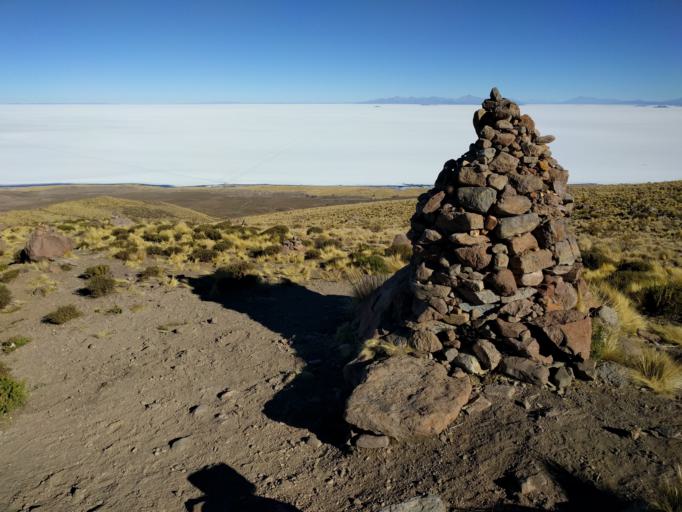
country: BO
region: Potosi
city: Colchani
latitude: -19.8686
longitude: -67.6352
